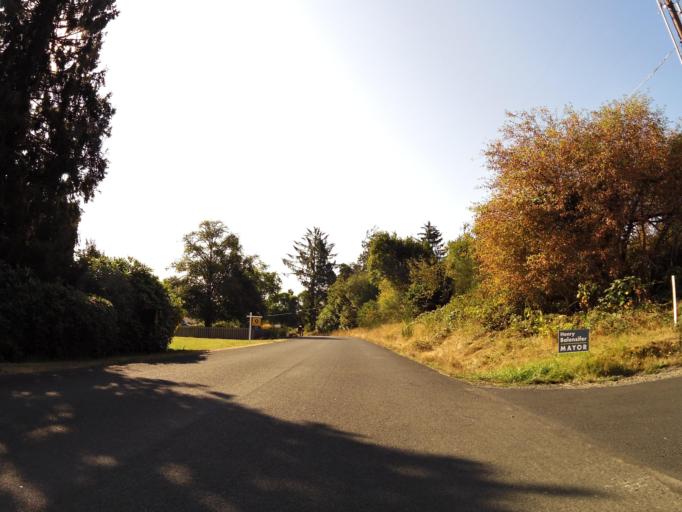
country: US
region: Oregon
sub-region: Clatsop County
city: Warrenton
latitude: 46.1340
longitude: -123.9337
